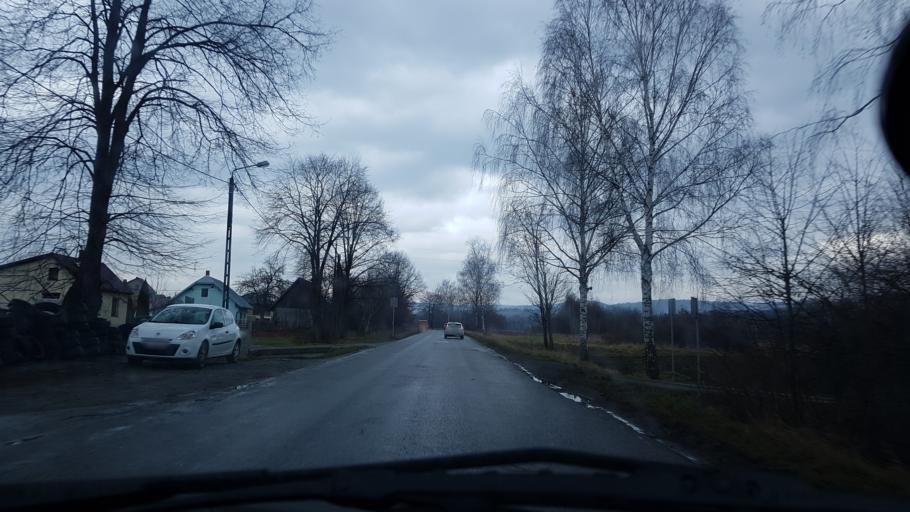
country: PL
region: Silesian Voivodeship
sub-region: Powiat zywiecki
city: Lekawica
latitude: 49.7110
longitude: 19.2385
